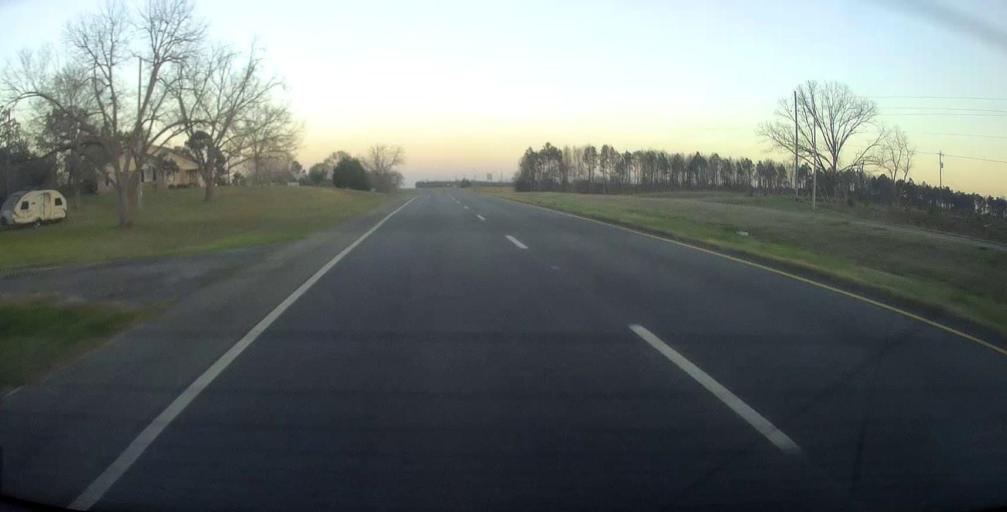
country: US
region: Georgia
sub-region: Dodge County
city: Eastman
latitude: 32.1588
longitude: -83.1476
